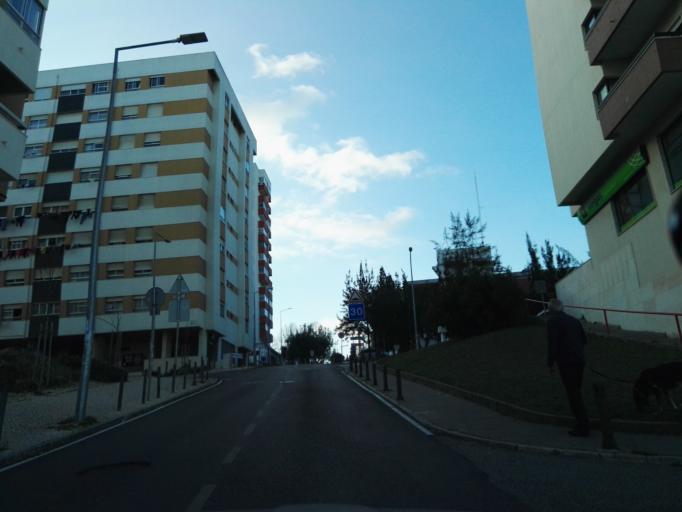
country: PT
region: Lisbon
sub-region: Vila Franca de Xira
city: Povoa de Santa Iria
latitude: 38.8619
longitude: -9.0661
